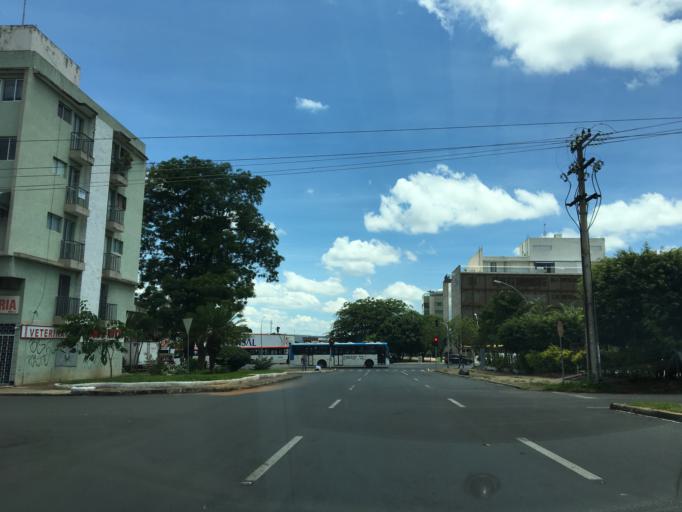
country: BR
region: Federal District
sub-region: Brasilia
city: Brasilia
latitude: -15.7453
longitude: -47.8977
